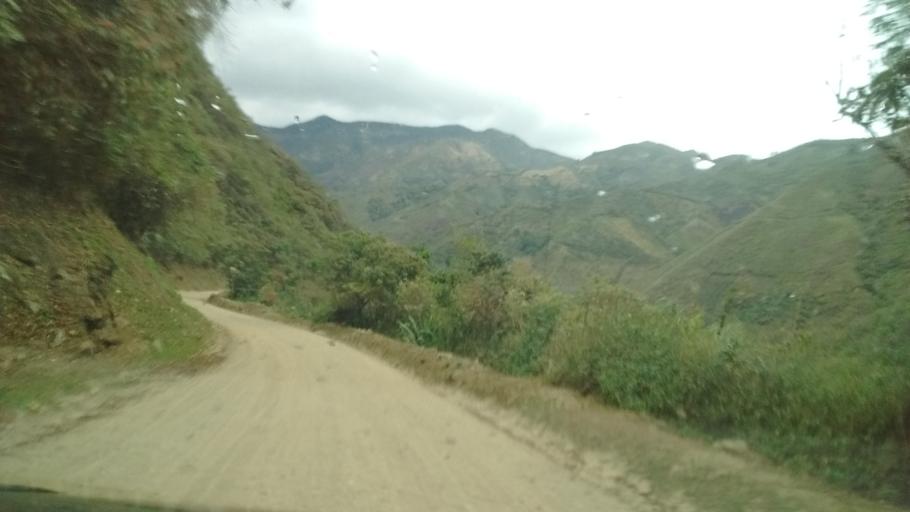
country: CO
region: Cauca
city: La Vega
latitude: 2.0342
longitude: -76.7969
